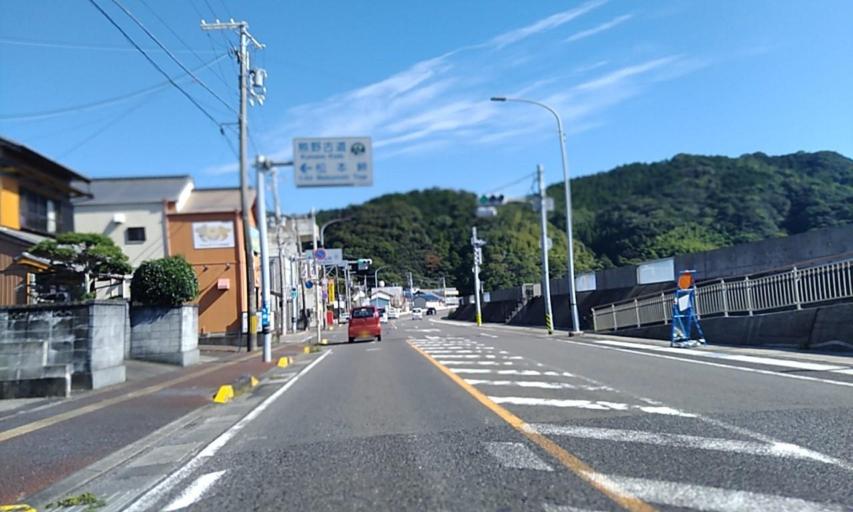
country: JP
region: Wakayama
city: Shingu
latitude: 33.8904
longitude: 136.1053
